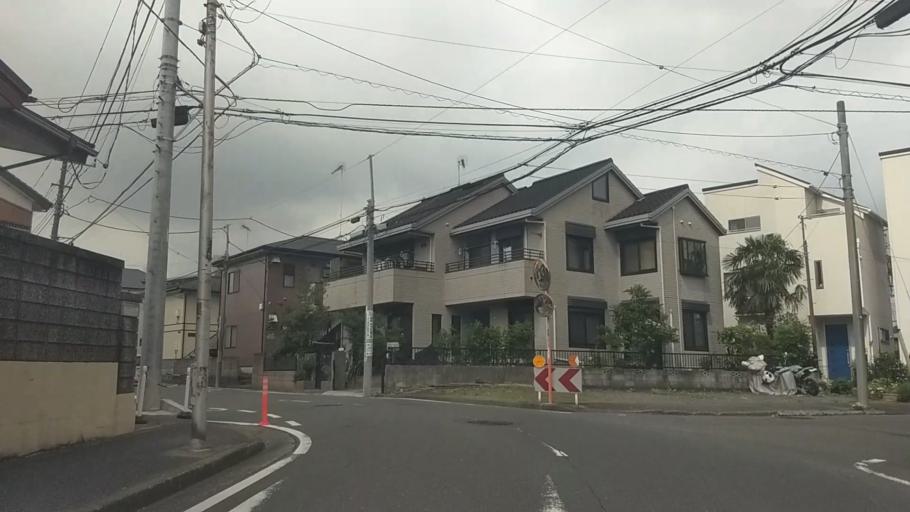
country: JP
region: Kanagawa
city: Kamakura
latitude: 35.3777
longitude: 139.5338
